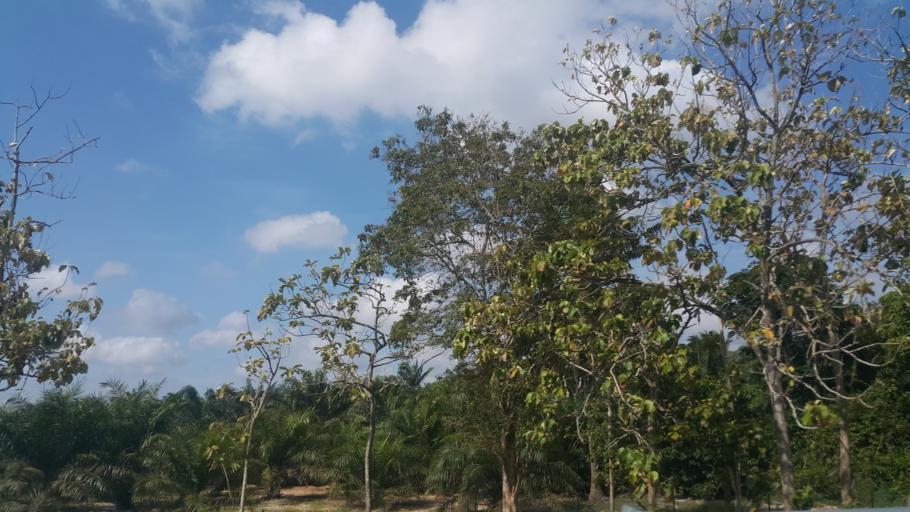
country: MY
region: Johor
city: Yong Peng
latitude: 1.9722
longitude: 103.1134
